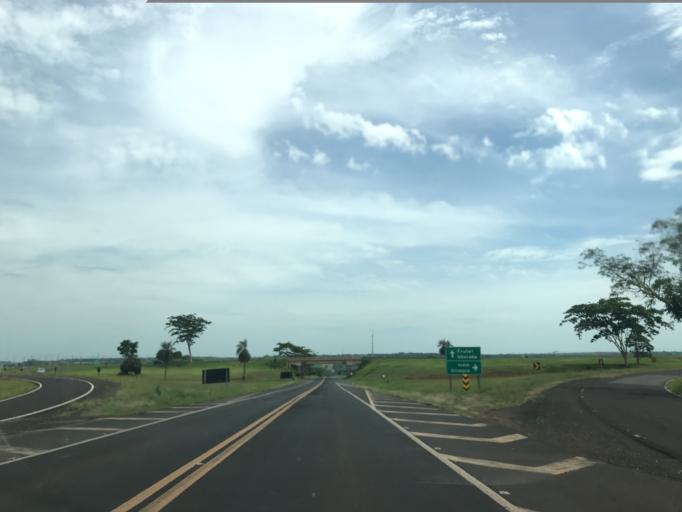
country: BR
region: Sao Paulo
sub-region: Nova Granada
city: Nova Granada
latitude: -20.3273
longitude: -49.2122
